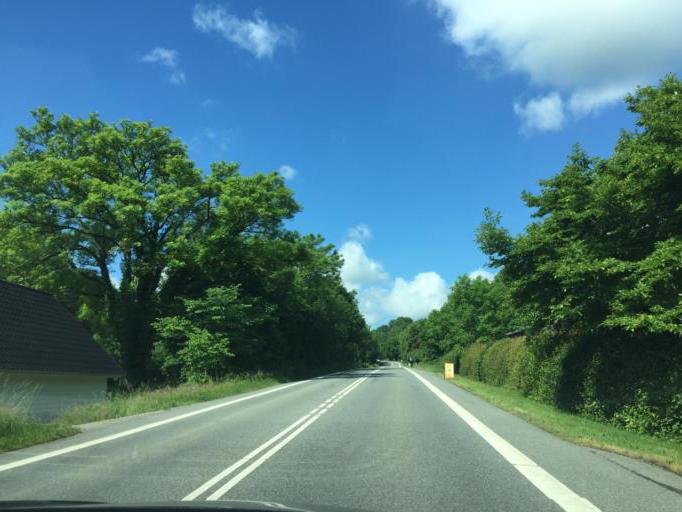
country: DK
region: South Denmark
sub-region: Fredericia Kommune
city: Taulov
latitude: 55.5300
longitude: 9.5745
